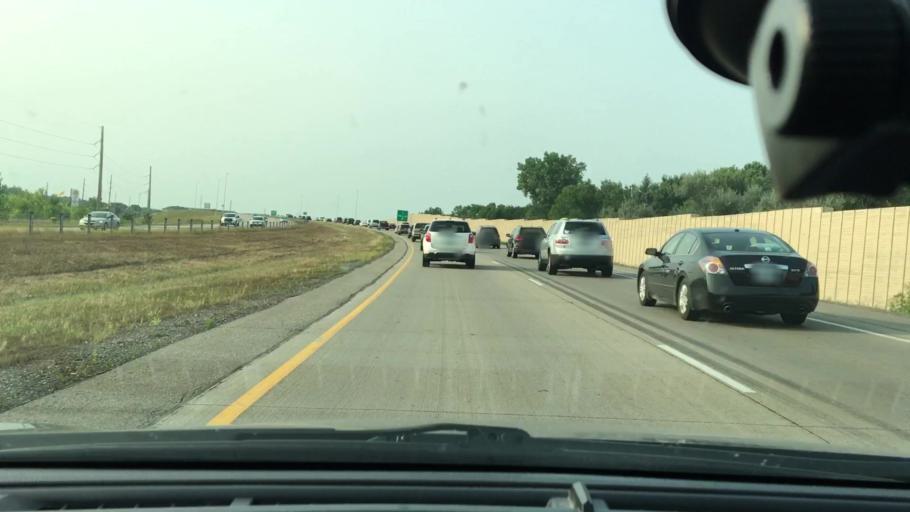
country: US
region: Minnesota
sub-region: Sherburne County
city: Elk River
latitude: 45.2746
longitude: -93.5566
